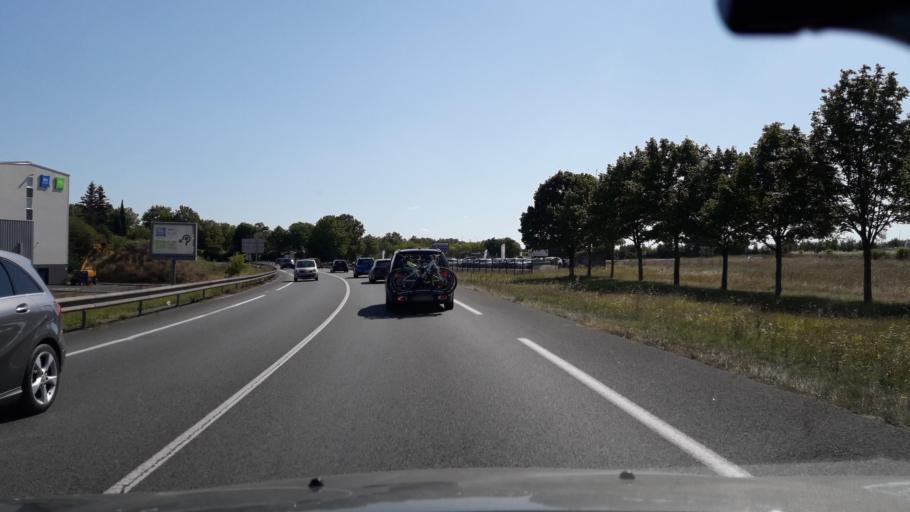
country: FR
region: Poitou-Charentes
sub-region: Departement de la Charente
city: Saint-Brice
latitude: 45.6813
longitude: -0.2961
